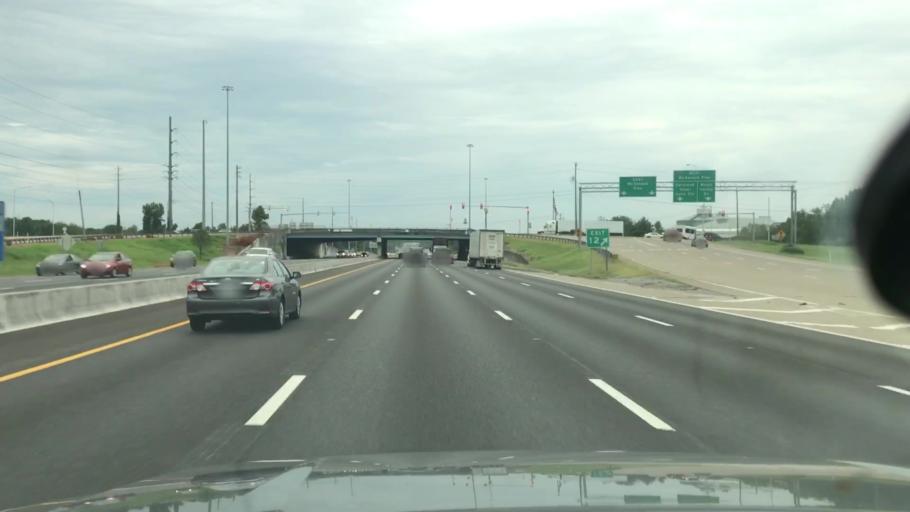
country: US
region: Tennessee
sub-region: Davidson County
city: Lakewood
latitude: 36.2187
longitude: -86.6931
